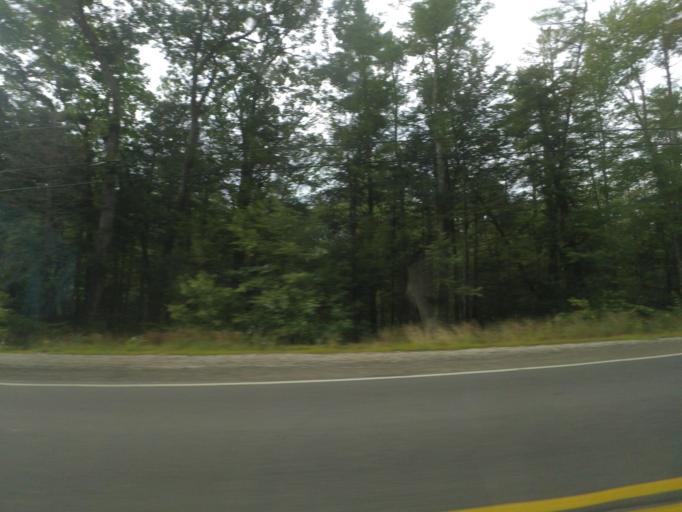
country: US
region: New Hampshire
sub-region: Strafford County
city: Barrington
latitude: 43.2327
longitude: -71.0596
